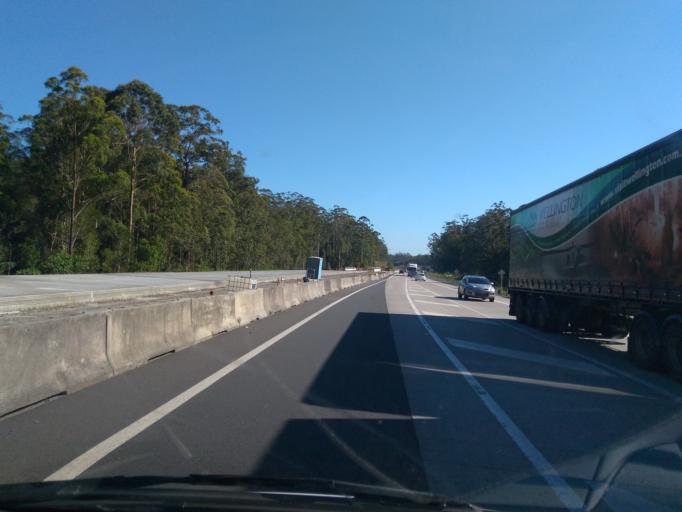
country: AU
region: New South Wales
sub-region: Port Macquarie-Hastings
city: North Shore
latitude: -31.2577
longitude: 152.8163
